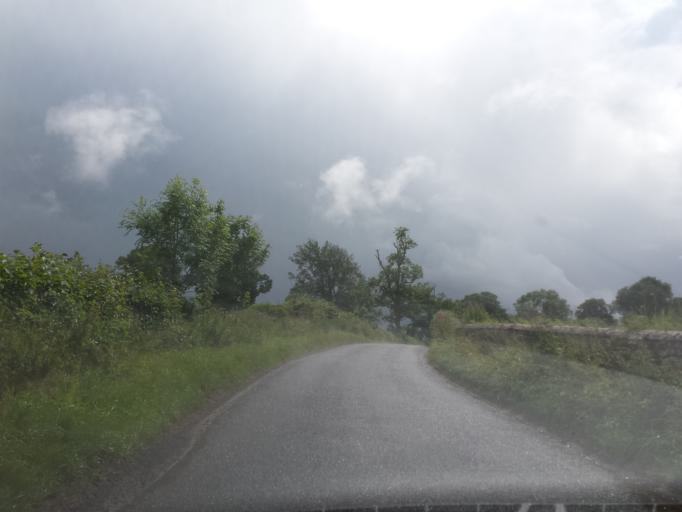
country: GB
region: Scotland
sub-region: The Scottish Borders
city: Saint Boswells
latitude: 55.5897
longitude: -2.6442
